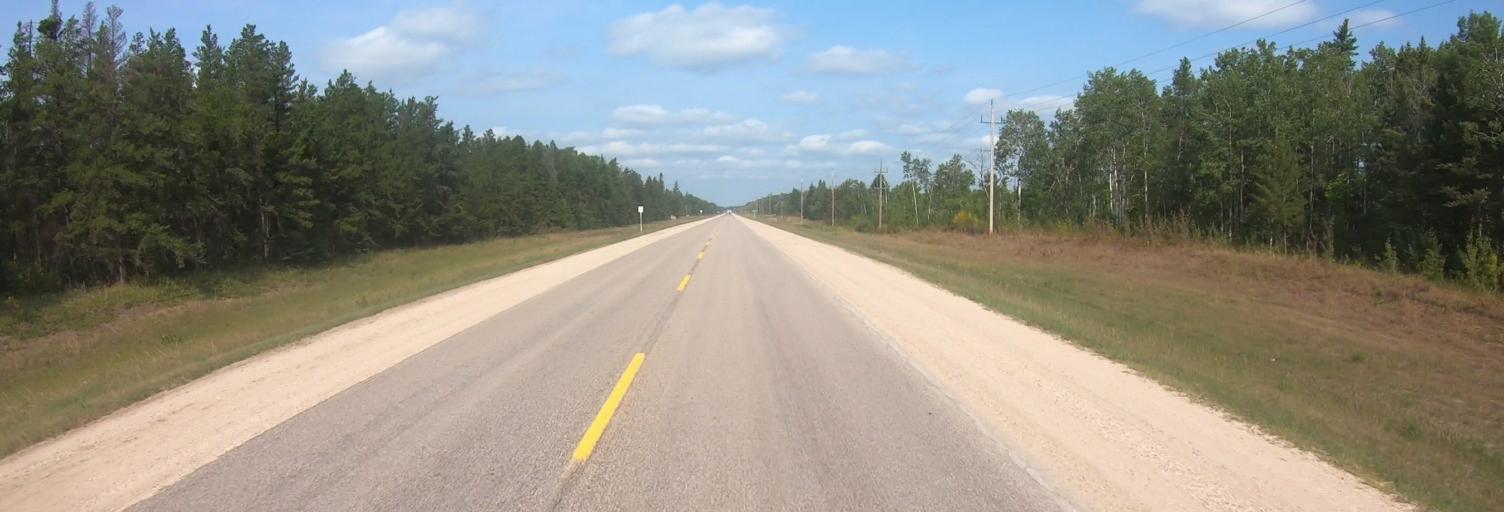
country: CA
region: Manitoba
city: La Broquerie
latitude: 49.1905
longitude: -96.2557
